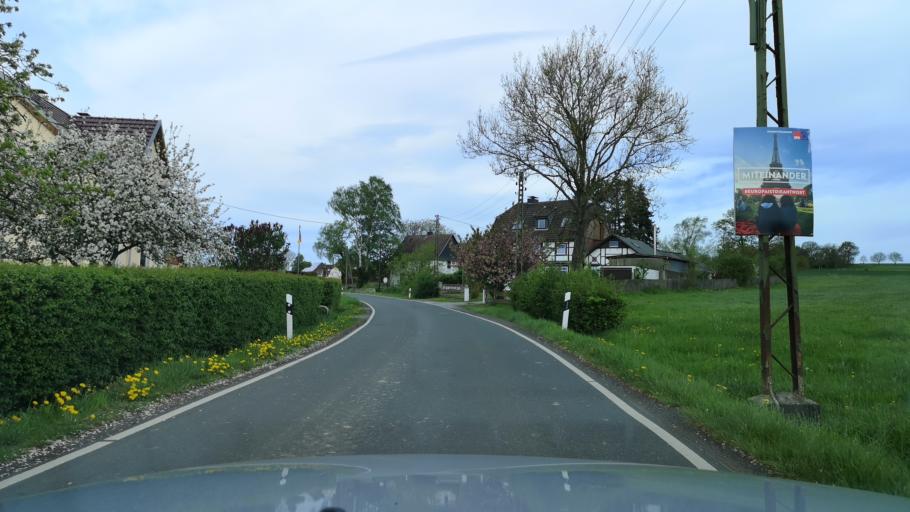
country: DE
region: North Rhine-Westphalia
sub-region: Regierungsbezirk Arnsberg
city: Holzwickede
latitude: 51.4810
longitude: 7.6690
